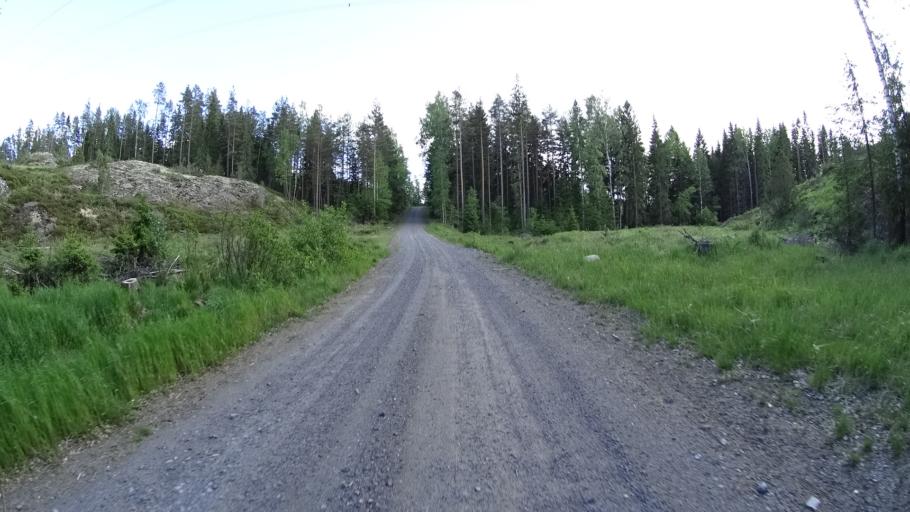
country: FI
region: Varsinais-Suomi
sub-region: Salo
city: Kisko
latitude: 60.1637
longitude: 23.4900
